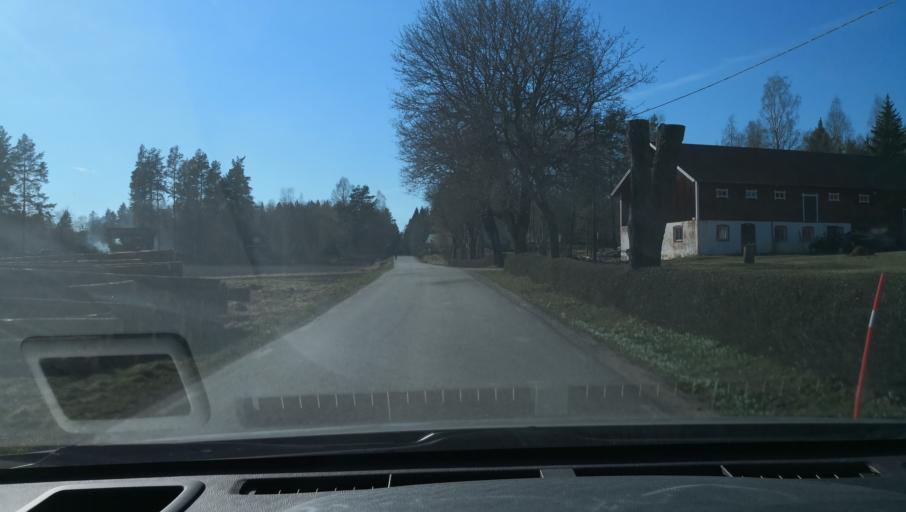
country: SE
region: Dalarna
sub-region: Avesta Kommun
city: Horndal
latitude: 60.0822
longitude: 16.4493
